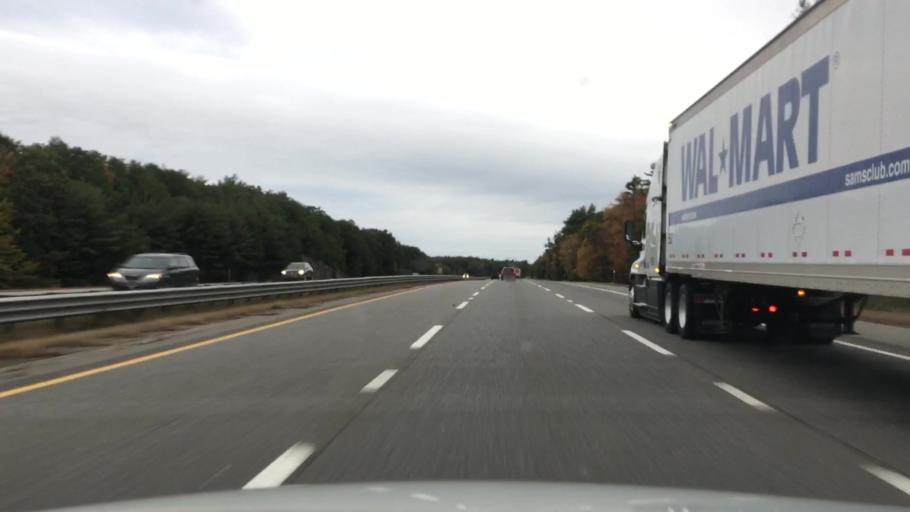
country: US
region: Maine
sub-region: York County
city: Cape Neddick
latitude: 43.1953
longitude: -70.6451
